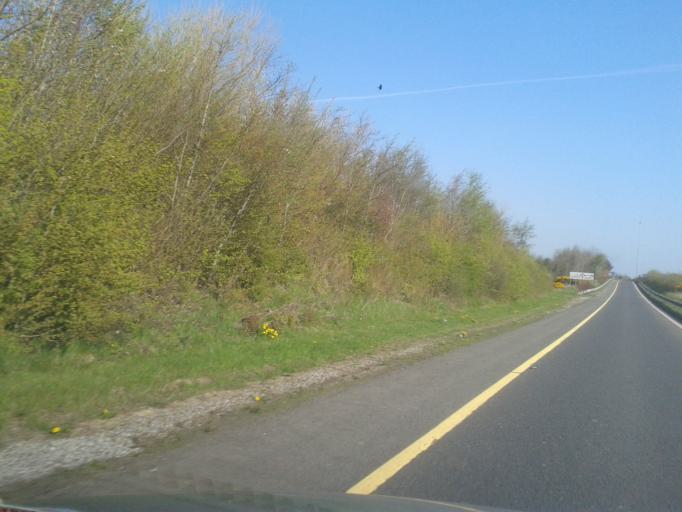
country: IE
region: Leinster
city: Balrothery
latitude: 53.5604
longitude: -6.2150
